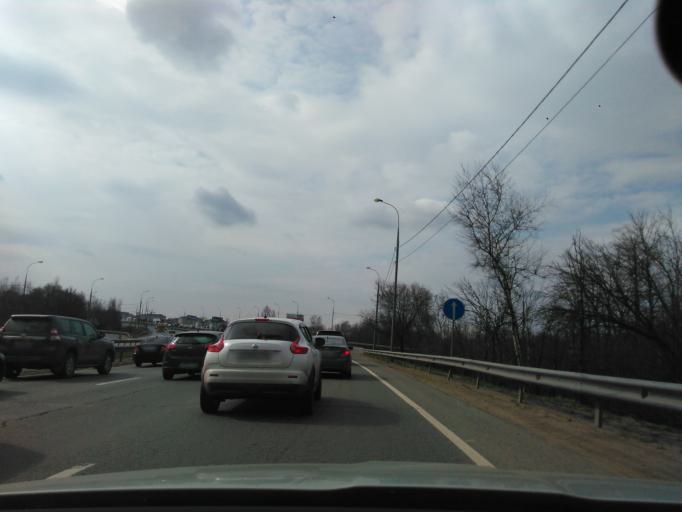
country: RU
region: Moskovskaya
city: Sheremet'yevskiy
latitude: 55.9788
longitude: 37.5244
